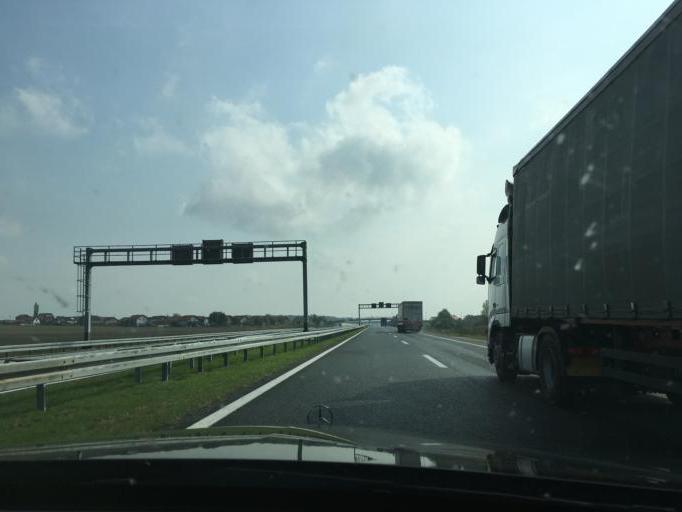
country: HR
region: Brodsko-Posavska
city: Bukovlje
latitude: 45.1810
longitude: 18.0526
